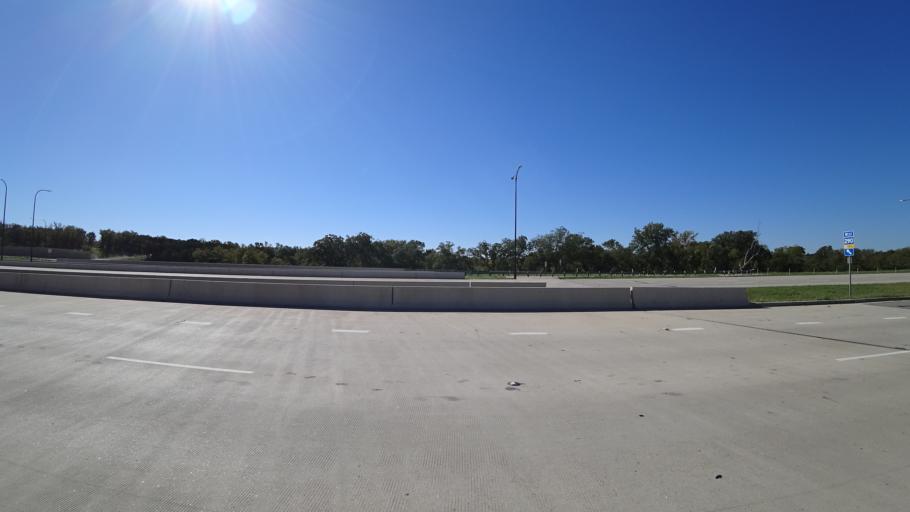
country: US
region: Texas
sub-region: Travis County
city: Manor
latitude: 30.3295
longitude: -97.6488
